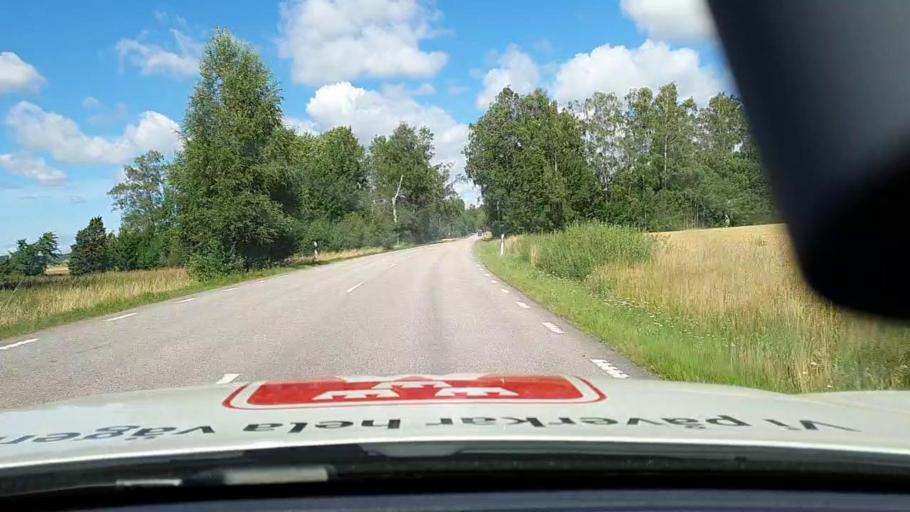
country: SE
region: Vaestra Goetaland
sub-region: Skovde Kommun
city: Stopen
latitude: 58.5539
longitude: 14.0035
